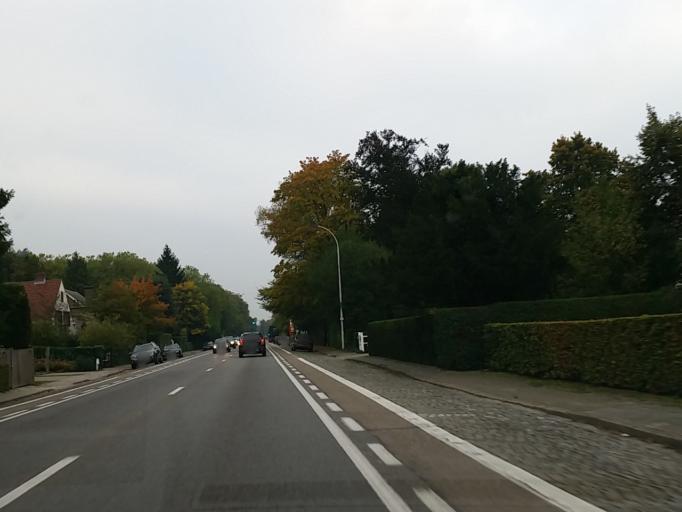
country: BE
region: Flanders
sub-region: Provincie Antwerpen
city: Kapellen
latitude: 51.2867
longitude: 4.4481
